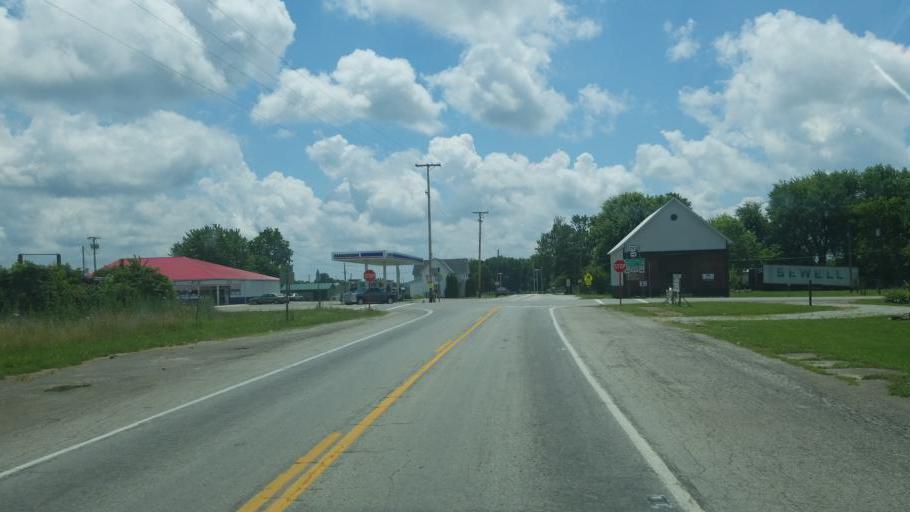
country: US
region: Ohio
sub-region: Highland County
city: Greenfield
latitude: 39.2203
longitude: -83.4217
